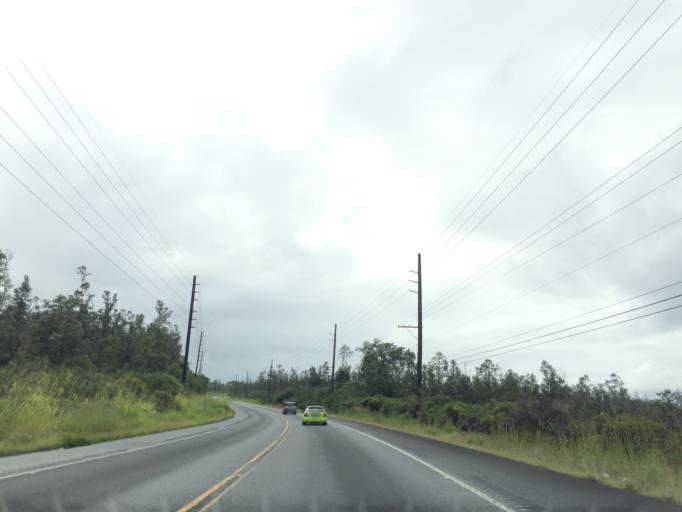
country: US
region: Hawaii
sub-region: Hawaii County
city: Ainaloa
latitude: 19.5279
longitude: -154.9708
